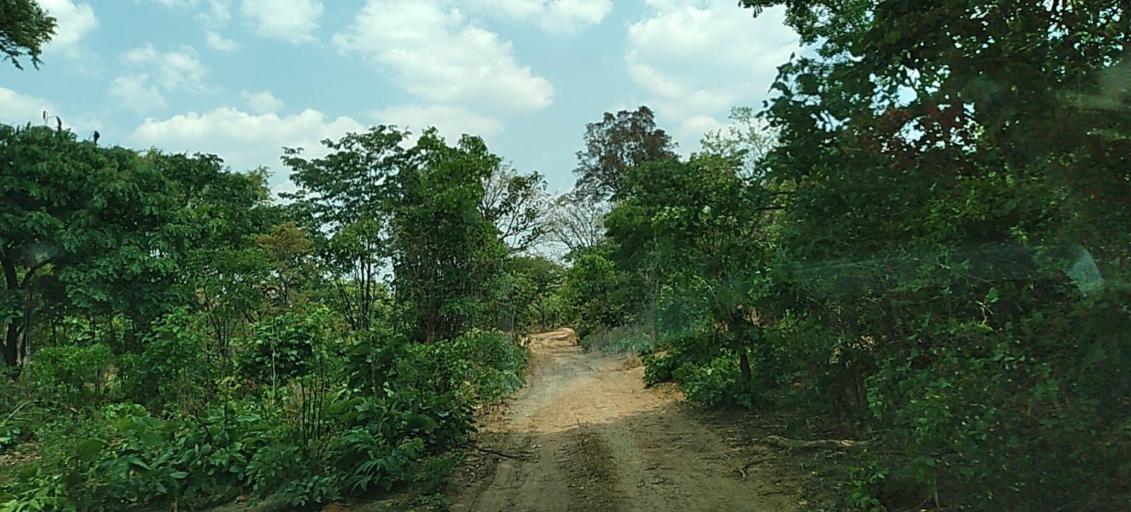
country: CD
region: Katanga
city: Kipushi
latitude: -12.0420
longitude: 27.4397
